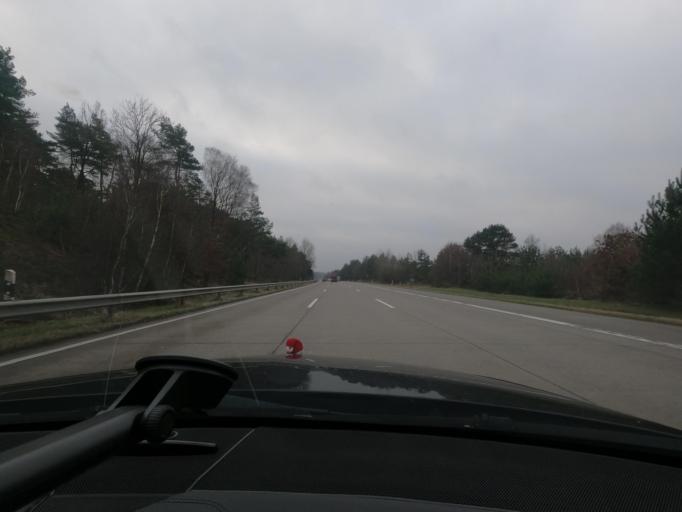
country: DE
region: Lower Saxony
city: Bispingen
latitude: 53.0469
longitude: 9.9502
